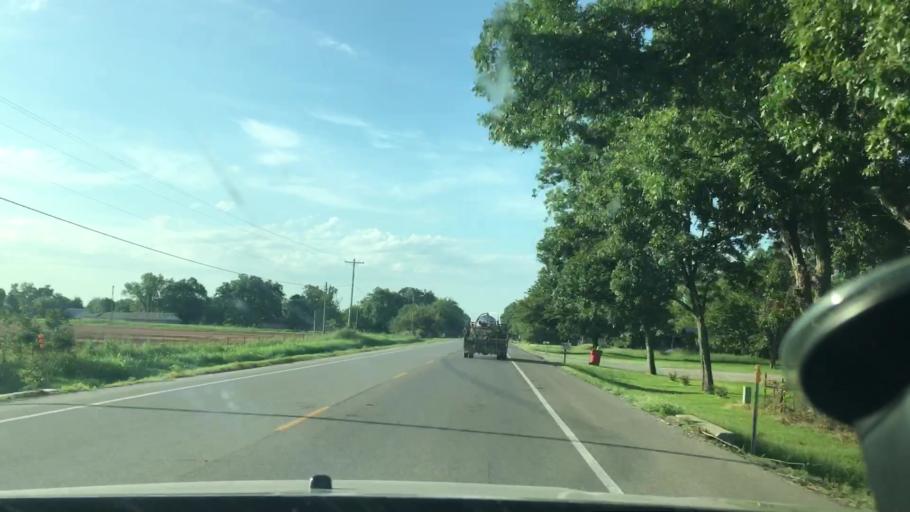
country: US
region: Oklahoma
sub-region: Garvin County
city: Wynnewood
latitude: 34.6753
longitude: -97.2076
